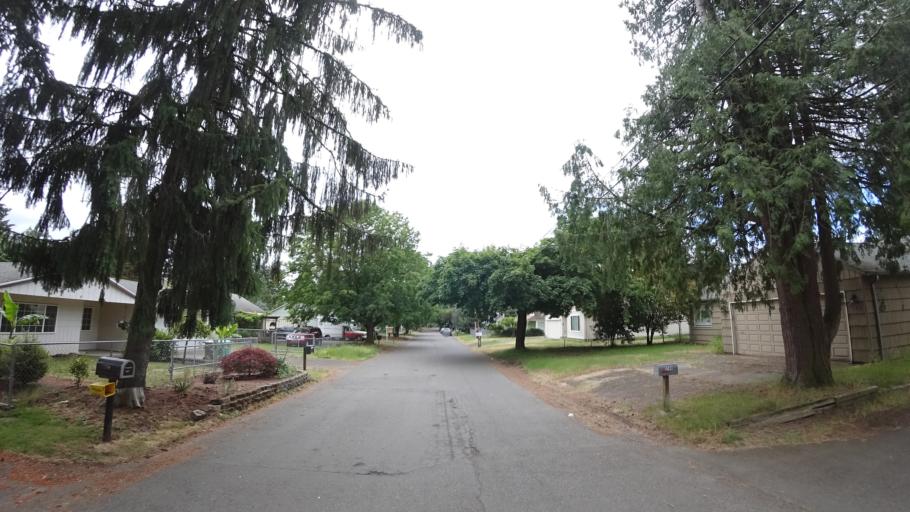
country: US
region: Oregon
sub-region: Multnomah County
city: Lents
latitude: 45.5020
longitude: -122.5285
